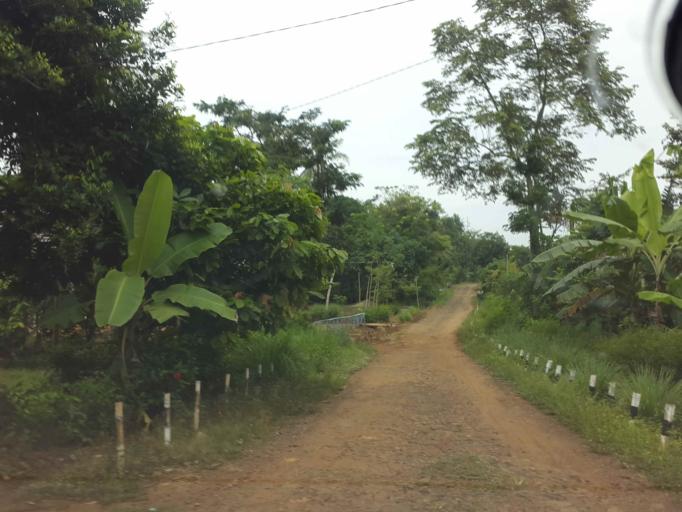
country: ID
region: Lampung
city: Sidorejo
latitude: -5.5563
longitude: 105.5314
